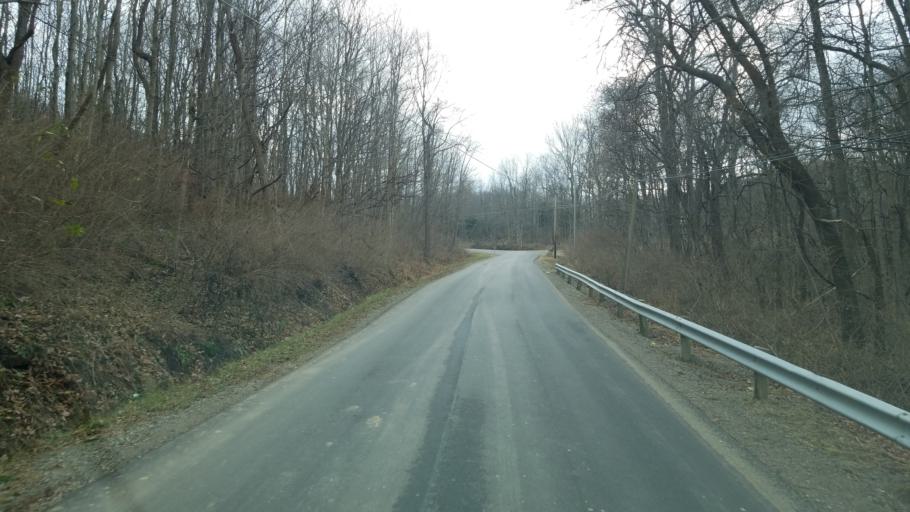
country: US
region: Ohio
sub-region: Highland County
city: Greenfield
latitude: 39.2076
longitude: -83.2693
